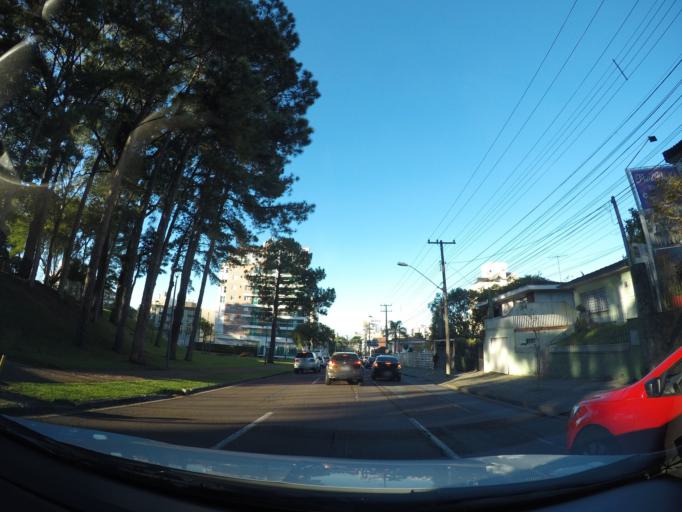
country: BR
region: Parana
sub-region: Curitiba
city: Curitiba
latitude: -25.4150
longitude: -49.2537
